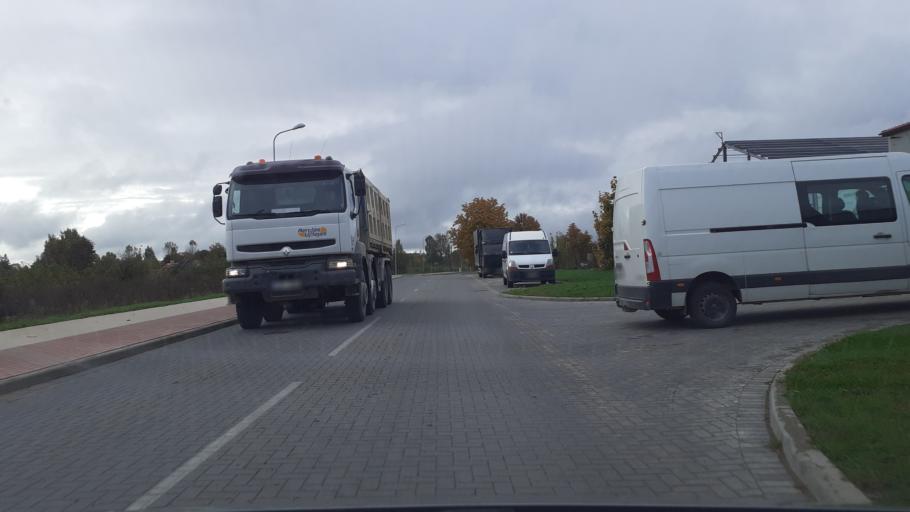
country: LV
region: Kuldigas Rajons
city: Kuldiga
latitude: 56.9815
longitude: 21.9492
